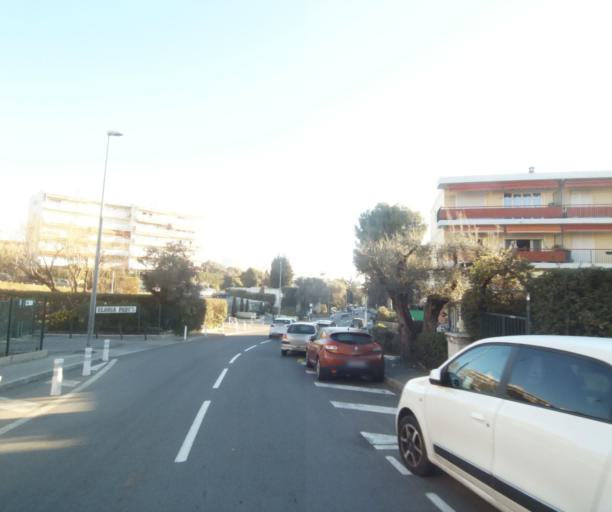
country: FR
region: Provence-Alpes-Cote d'Azur
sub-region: Departement des Alpes-Maritimes
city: Biot
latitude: 43.5906
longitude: 7.0979
